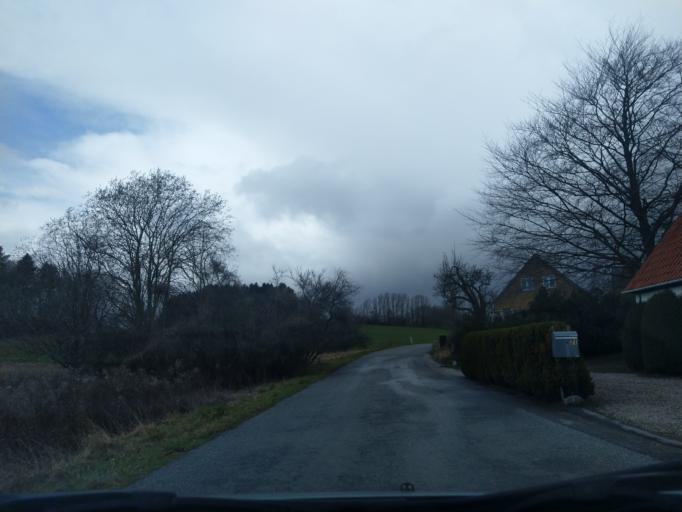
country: DK
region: Zealand
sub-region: Soro Kommune
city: Frederiksberg
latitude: 55.3596
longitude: 11.5722
